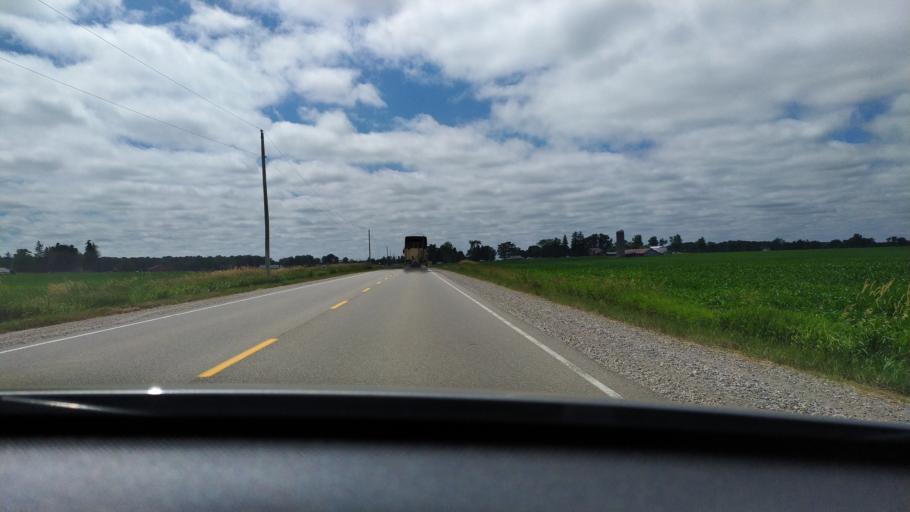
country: CA
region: Ontario
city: Stratford
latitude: 43.3162
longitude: -80.9764
